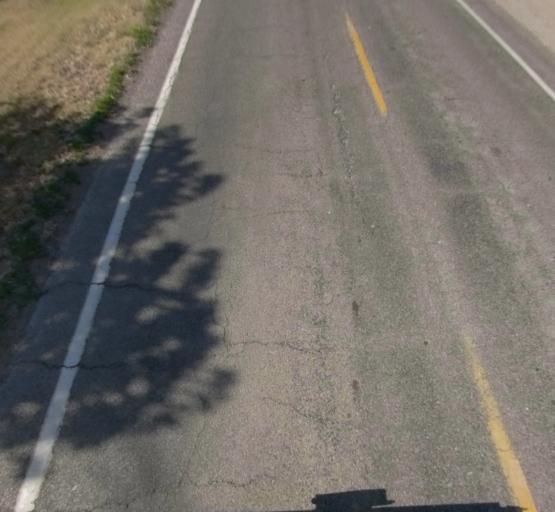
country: US
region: California
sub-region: Madera County
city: Fairmead
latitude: 37.0512
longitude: -120.2568
